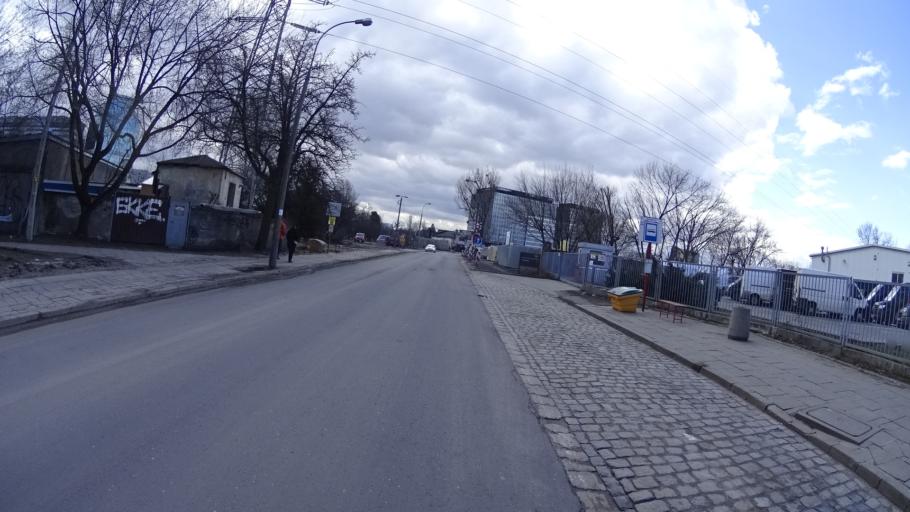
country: PL
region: Masovian Voivodeship
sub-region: Warszawa
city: Ochota
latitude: 52.2231
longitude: 20.9693
